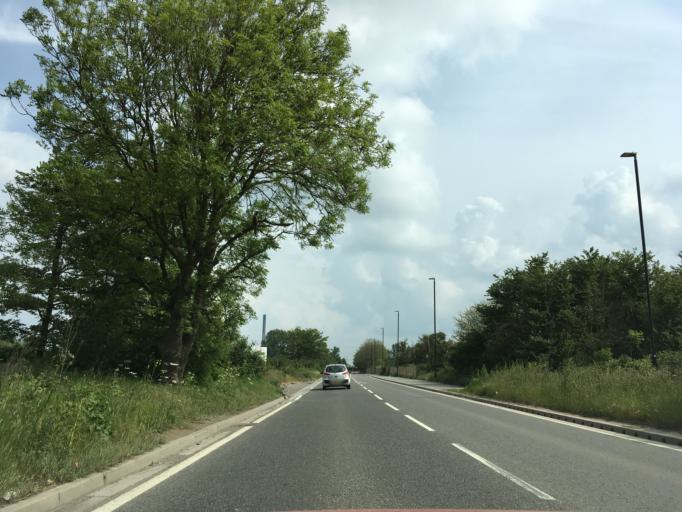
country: GB
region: England
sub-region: South Gloucestershire
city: Severn Beach
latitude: 51.5304
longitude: -2.6739
